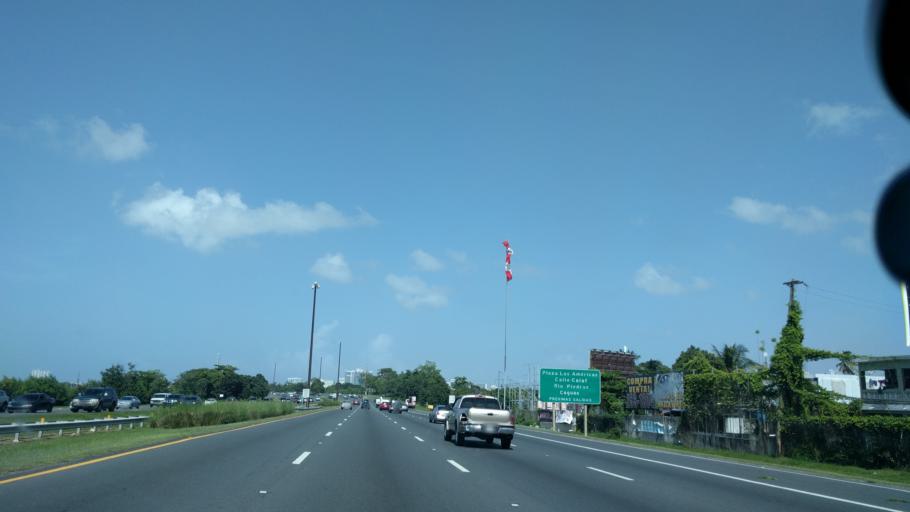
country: PR
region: Catano
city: Catano
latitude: 18.4189
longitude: -66.0870
